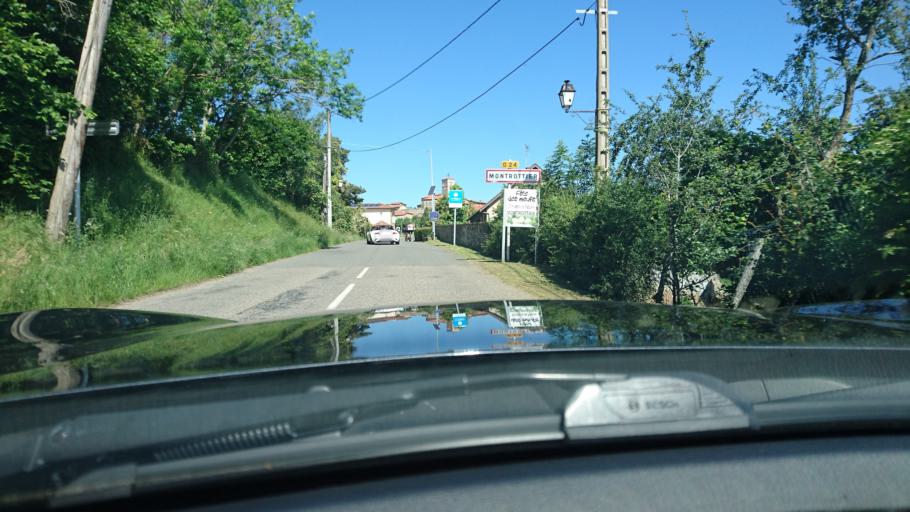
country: FR
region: Rhone-Alpes
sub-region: Departement du Rhone
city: Montrottier
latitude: 45.7880
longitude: 4.4713
